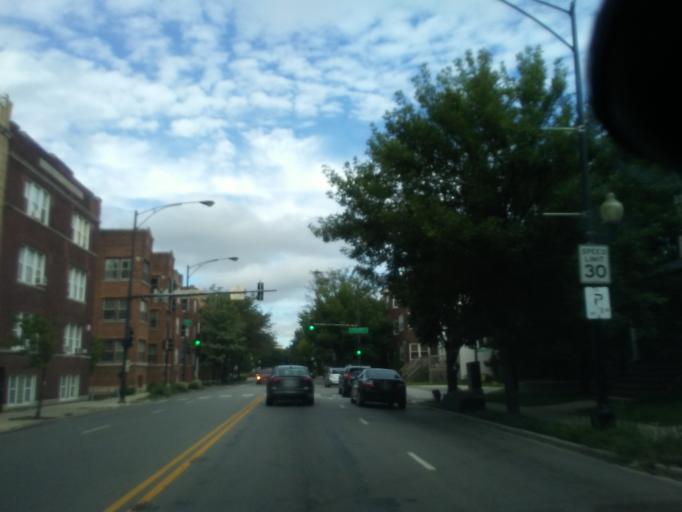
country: US
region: Illinois
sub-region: Cook County
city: Evanston
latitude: 41.9849
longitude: -87.6621
